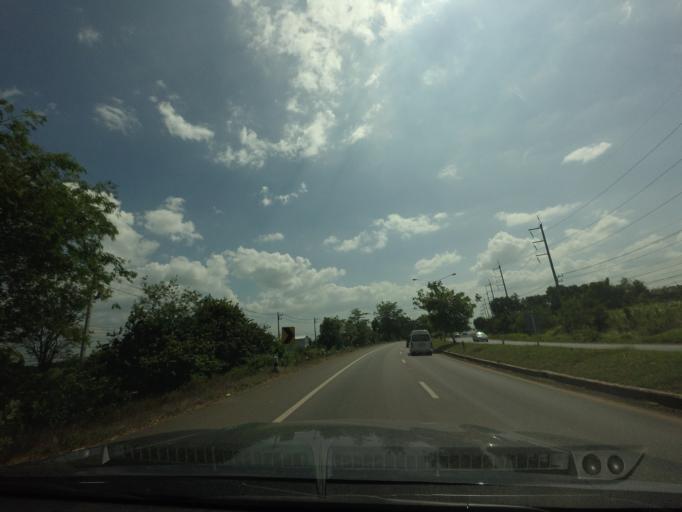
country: TH
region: Phetchabun
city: Nong Phai
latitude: 15.8998
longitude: 101.0278
